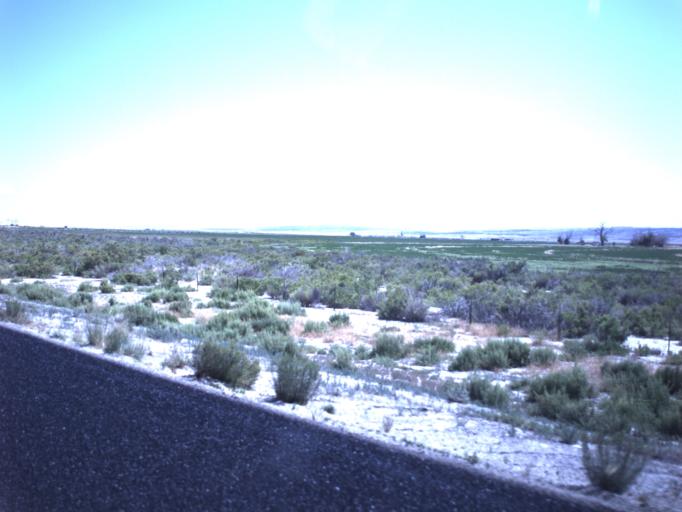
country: US
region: Utah
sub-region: Emery County
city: Ferron
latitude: 38.9906
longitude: -111.1685
